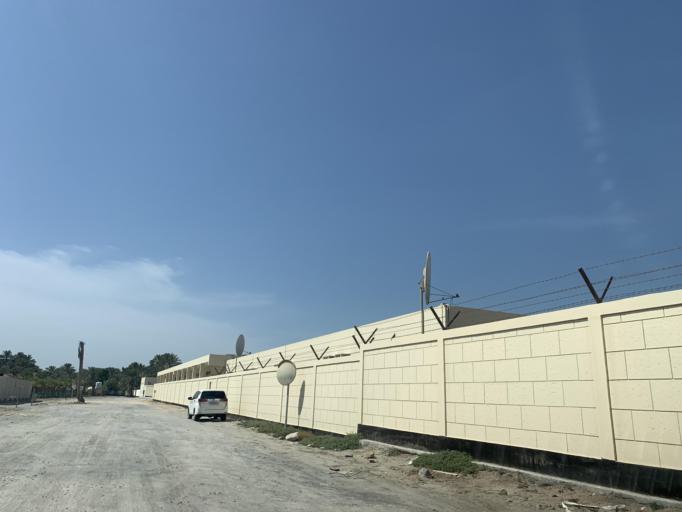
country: BH
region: Central Governorate
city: Madinat Hamad
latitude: 26.1835
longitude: 50.4690
